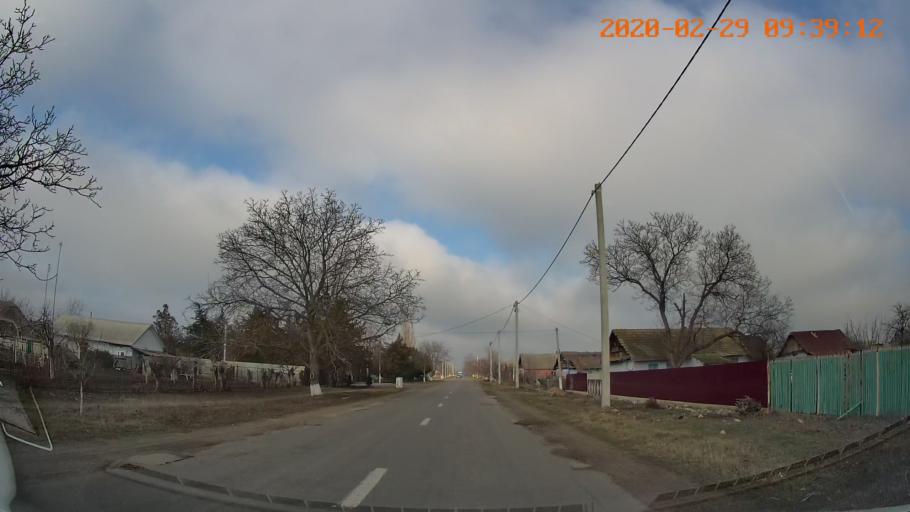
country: MD
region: Telenesti
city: Crasnoe
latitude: 46.6344
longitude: 29.8575
